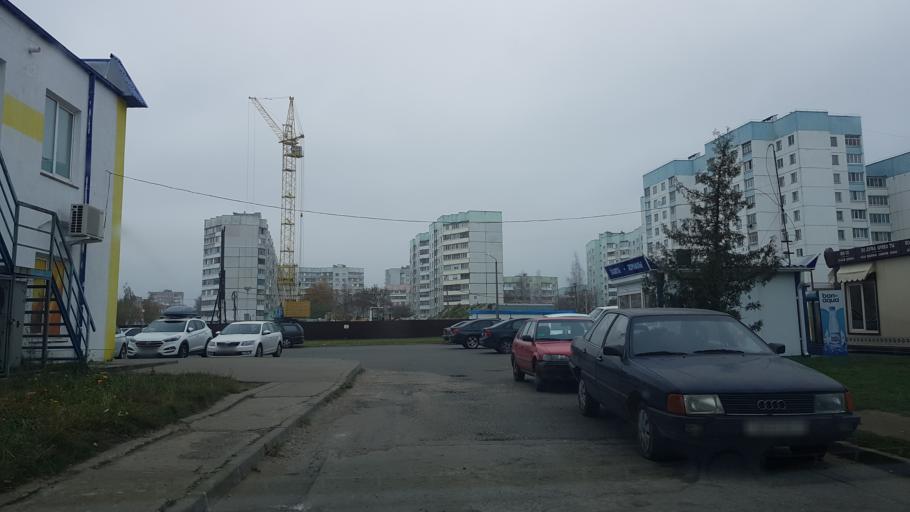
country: BY
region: Mogilev
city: Babruysk
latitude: 53.1871
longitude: 29.2262
